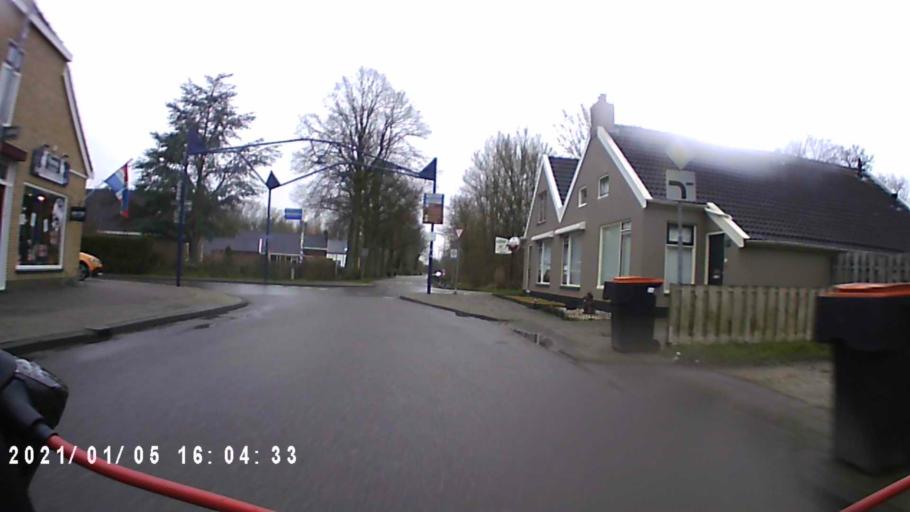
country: NL
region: Groningen
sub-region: Gemeente  Oldambt
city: Winschoten
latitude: 53.1987
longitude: 7.0818
